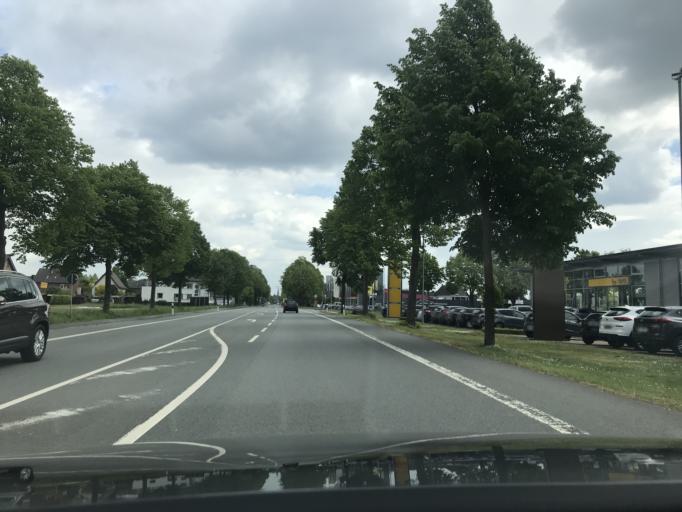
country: DE
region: North Rhine-Westphalia
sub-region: Regierungsbezirk Detmold
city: Rheda-Wiedenbruck
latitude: 51.8624
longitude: 8.2736
